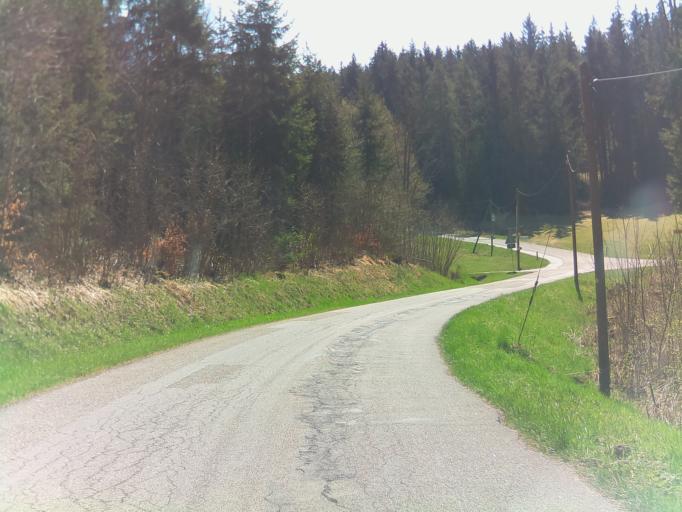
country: DE
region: Bavaria
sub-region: Upper Palatinate
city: Kastl
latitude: 49.3867
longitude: 11.6868
